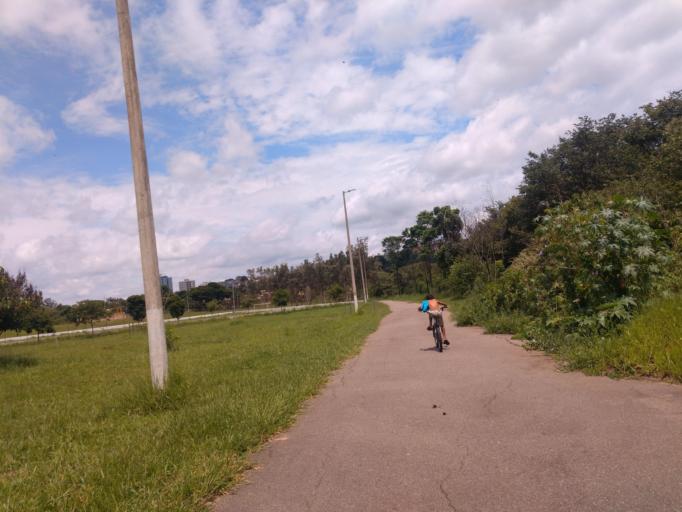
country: BR
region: Minas Gerais
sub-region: Tres Coracoes
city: Tres Coracoes
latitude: -21.7003
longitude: -45.2454
